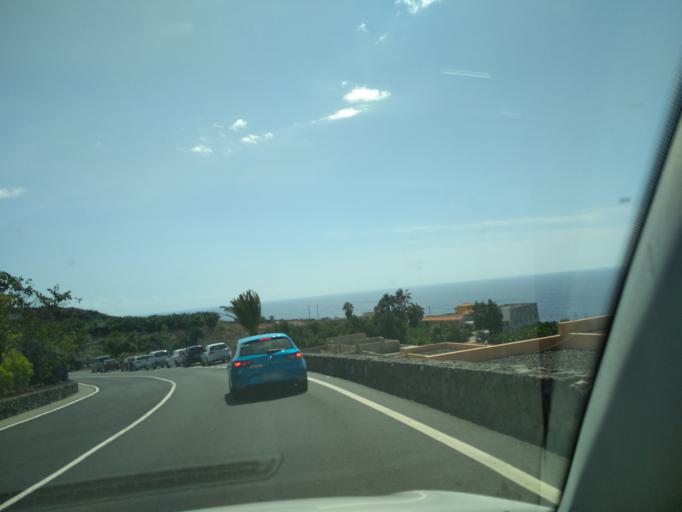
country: ES
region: Canary Islands
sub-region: Provincia de Santa Cruz de Tenerife
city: Santiago del Teide
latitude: 28.2401
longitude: -16.8372
